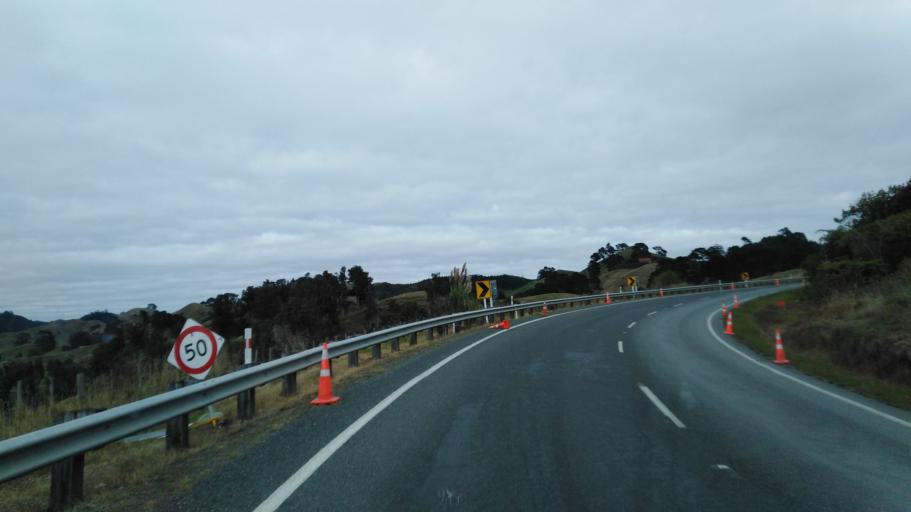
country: NZ
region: Bay of Plenty
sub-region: Western Bay of Plenty District
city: Waihi Beach
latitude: -37.4111
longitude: 175.9288
